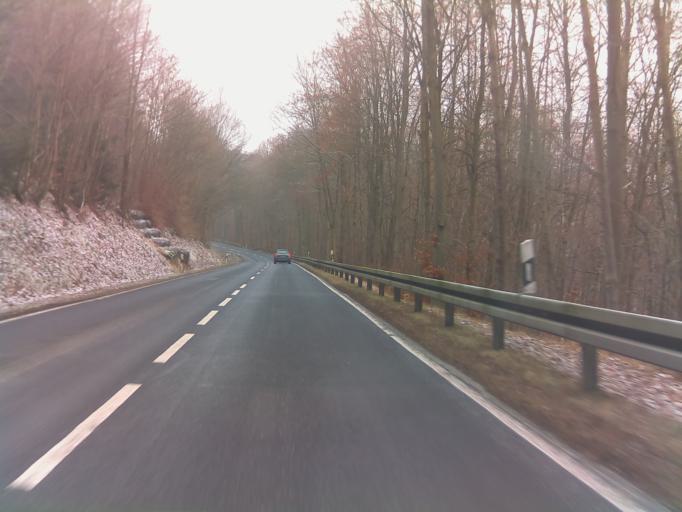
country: DE
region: Bavaria
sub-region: Regierungsbezirk Unterfranken
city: Bad Bruckenau
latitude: 50.3032
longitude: 9.7621
